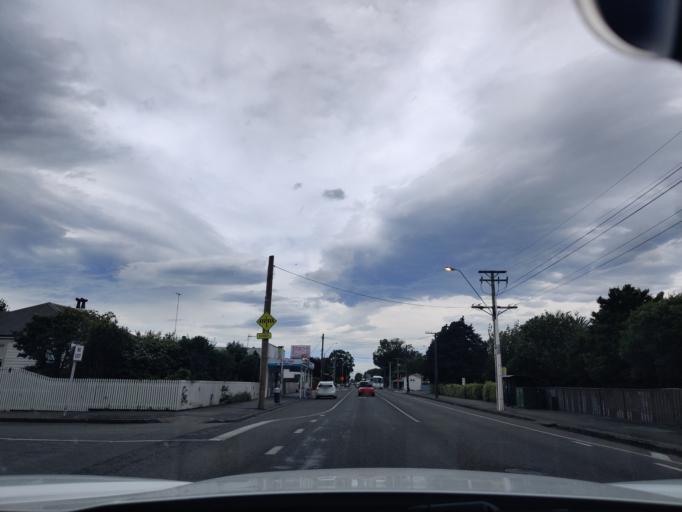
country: NZ
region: Wellington
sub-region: Masterton District
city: Masterton
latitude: -41.0309
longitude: 175.5218
